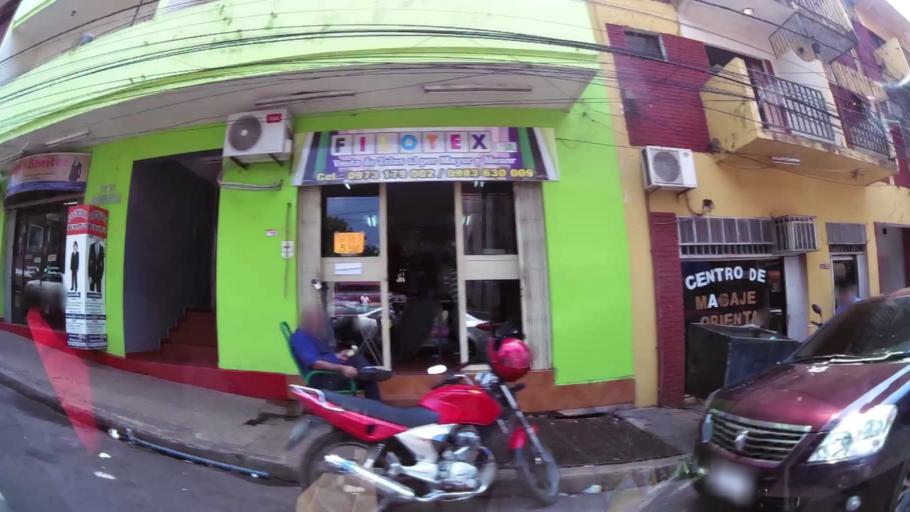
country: PY
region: Alto Parana
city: Ciudad del Este
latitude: -25.5126
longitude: -54.6125
